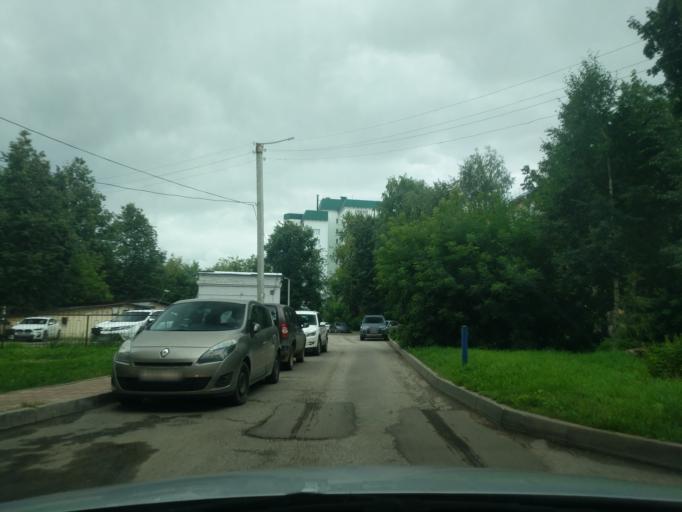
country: RU
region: Kirov
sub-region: Kirovo-Chepetskiy Rayon
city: Kirov
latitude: 58.5960
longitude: 49.6828
